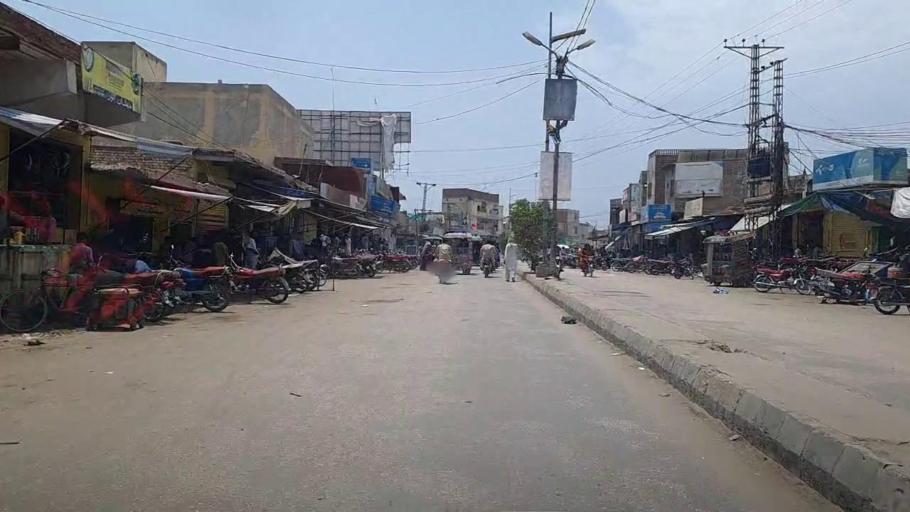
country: PK
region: Sindh
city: Khairpur
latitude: 28.0520
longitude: 69.7000
